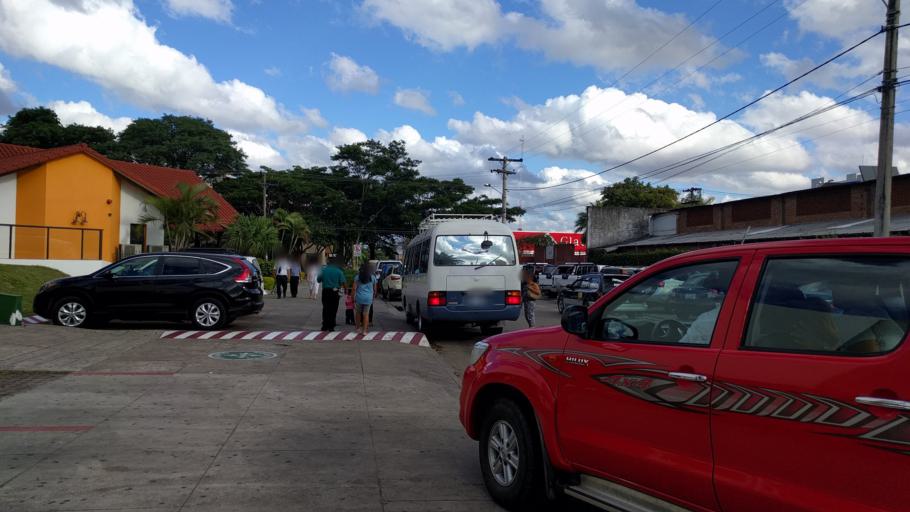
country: BO
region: Santa Cruz
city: Santa Cruz de la Sierra
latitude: -17.7773
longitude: -63.1644
